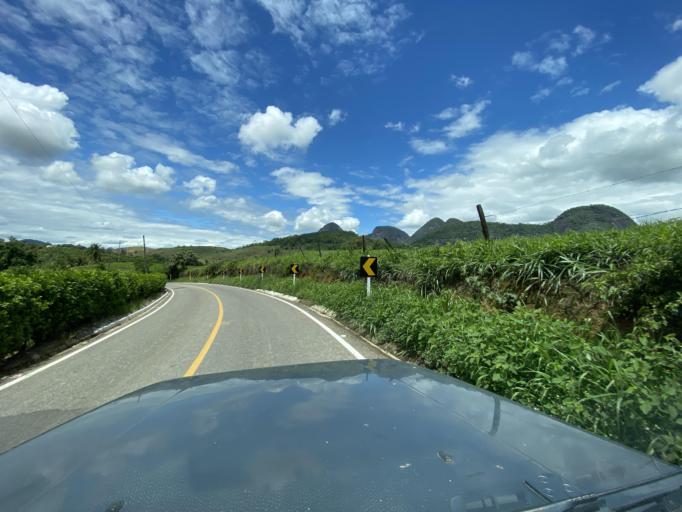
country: BR
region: Espirito Santo
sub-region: Jeronimo Monteiro
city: Jeronimo Monteiro
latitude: -20.7796
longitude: -41.3871
